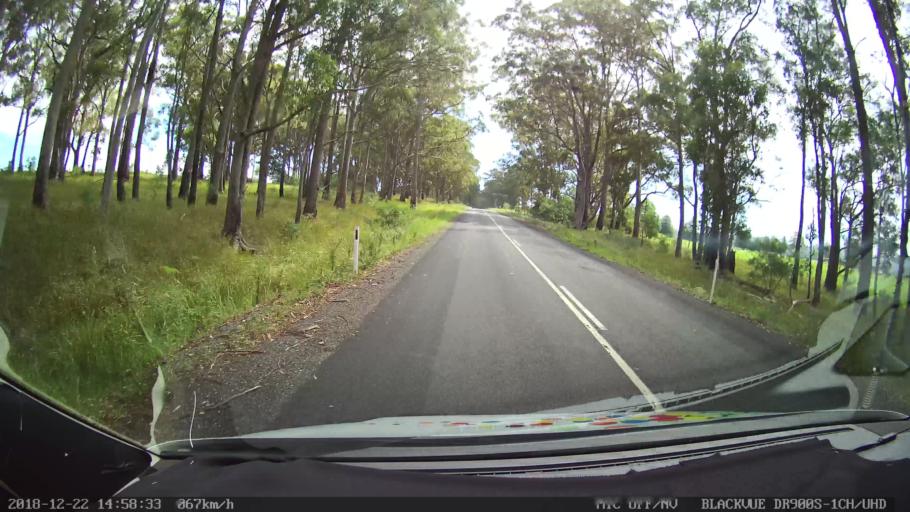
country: AU
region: New South Wales
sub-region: Bellingen
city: Dorrigo
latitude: -30.2408
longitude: 152.4900
